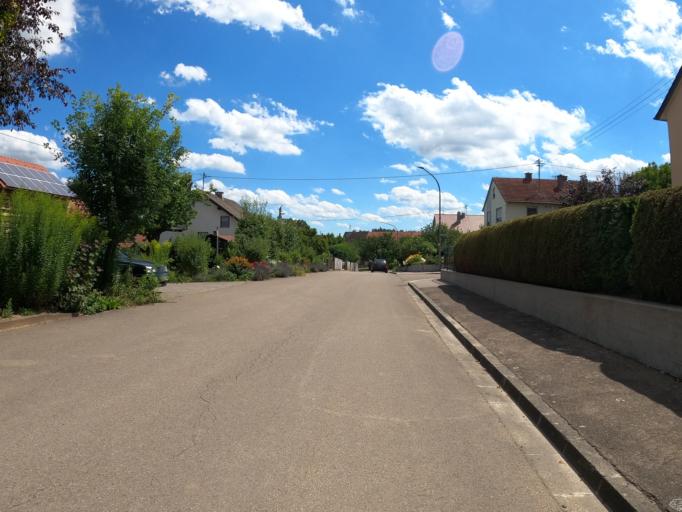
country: DE
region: Bavaria
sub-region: Swabia
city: Pfaffenhofen an der Roth
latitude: 48.3994
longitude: 10.1777
